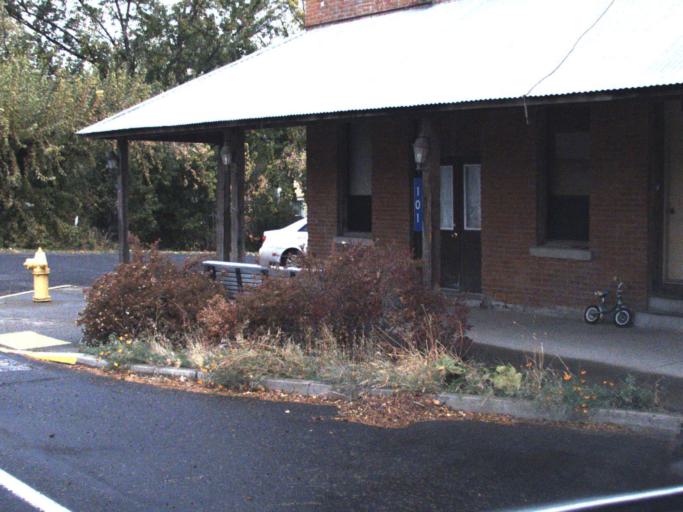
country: US
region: Washington
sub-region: Asotin County
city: Clarkston
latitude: 46.5392
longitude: -117.0874
